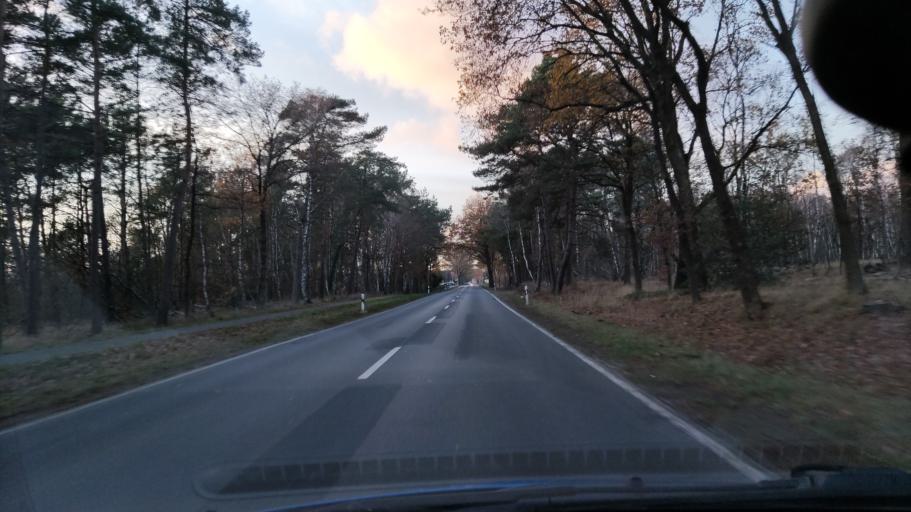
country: DE
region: Lower Saxony
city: Schneverdingen
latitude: 53.1072
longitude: 9.8159
